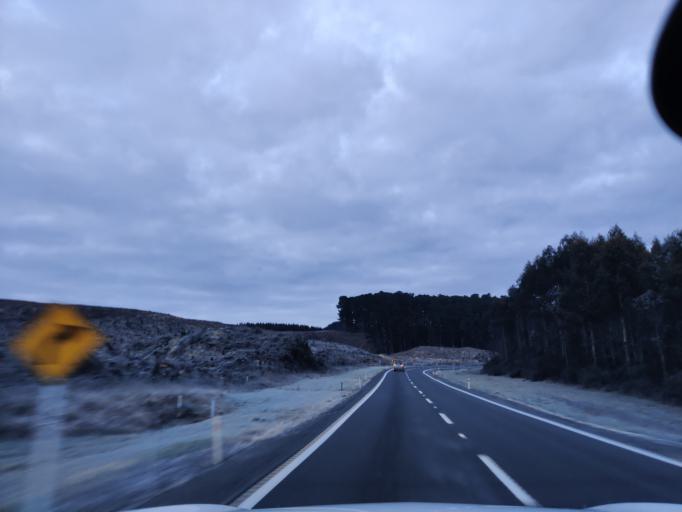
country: NZ
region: Waikato
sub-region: South Waikato District
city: Tokoroa
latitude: -38.4081
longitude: 176.0517
